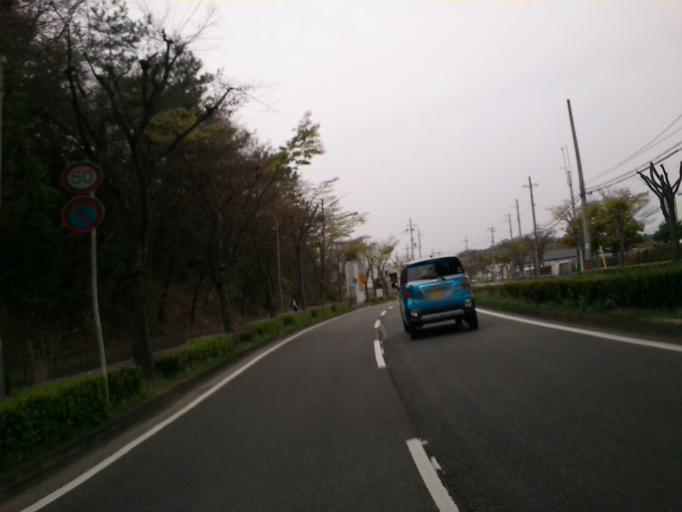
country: JP
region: Kyoto
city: Tanabe
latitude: 34.8287
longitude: 135.7502
